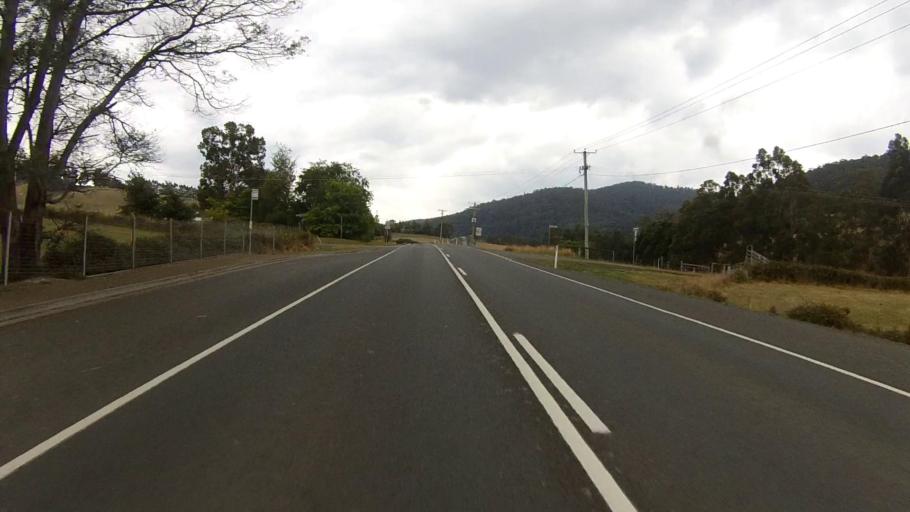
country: AU
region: Tasmania
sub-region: Huon Valley
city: Cygnet
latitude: -43.1500
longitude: 147.0695
